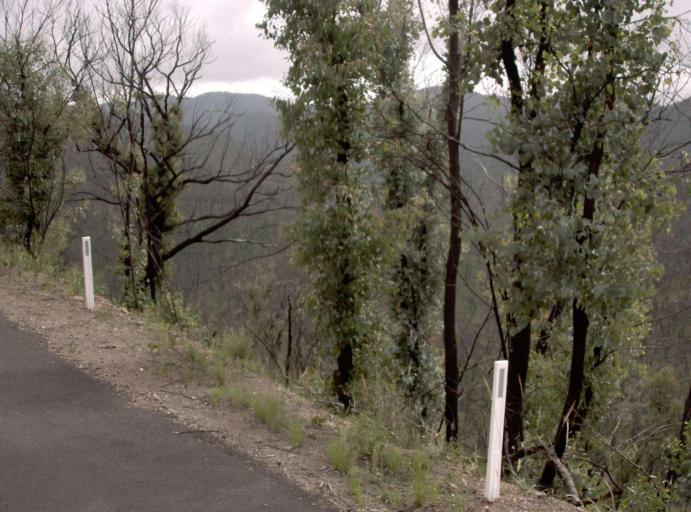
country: AU
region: Victoria
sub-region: Wellington
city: Heyfield
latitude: -37.7286
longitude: 146.6696
